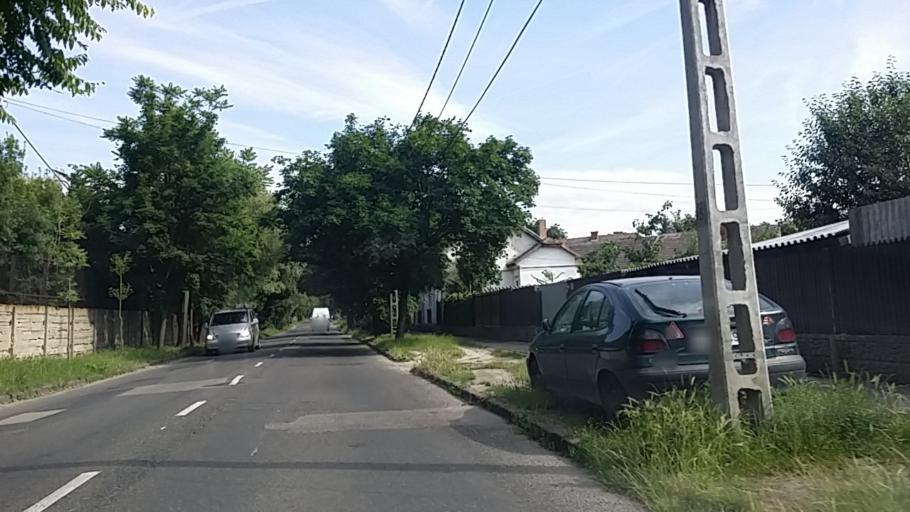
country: HU
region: Budapest
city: Budapest XXI. keruelet
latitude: 47.4308
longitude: 19.0802
